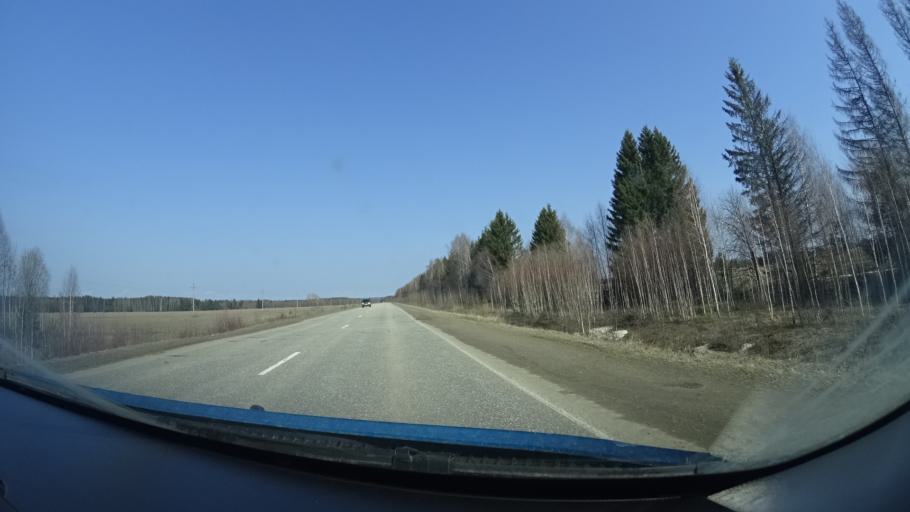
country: RU
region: Perm
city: Osa
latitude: 57.3420
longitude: 55.5890
